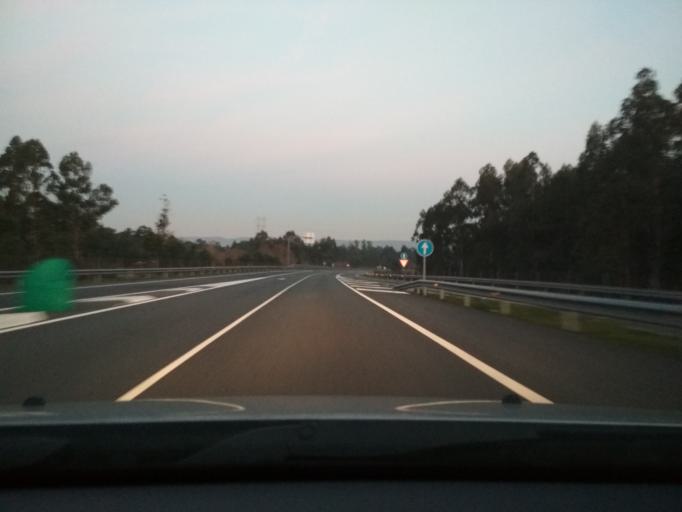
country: ES
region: Galicia
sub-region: Provincia da Coruna
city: Santiago de Compostela
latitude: 42.8484
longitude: -8.5957
